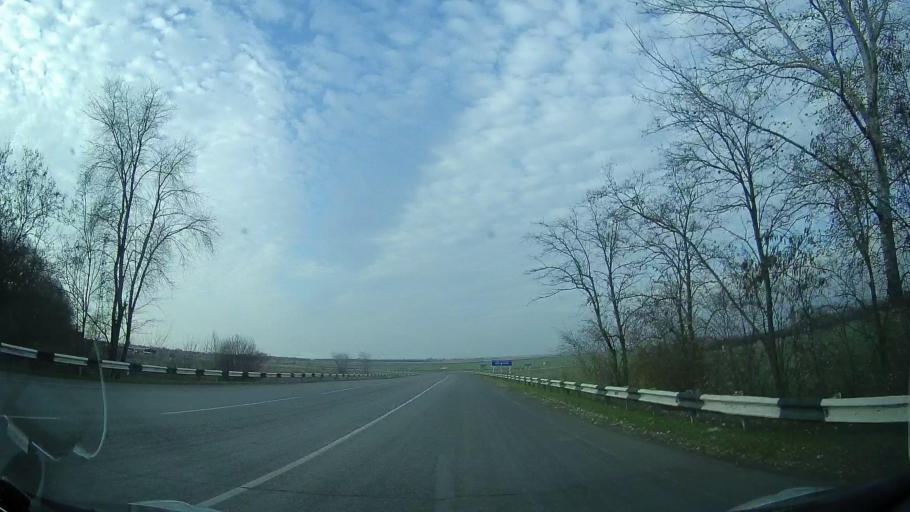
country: RU
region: Rostov
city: Bagayevskaya
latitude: 47.1640
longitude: 40.2736
